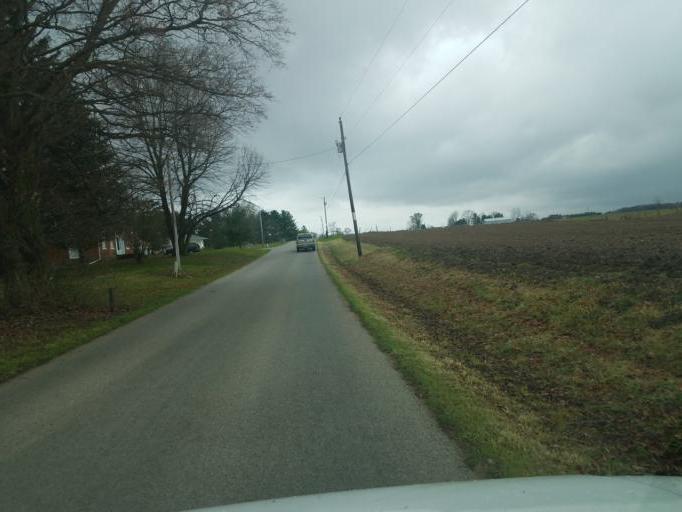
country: US
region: Ohio
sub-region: Morrow County
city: Mount Gilead
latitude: 40.5788
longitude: -82.8181
